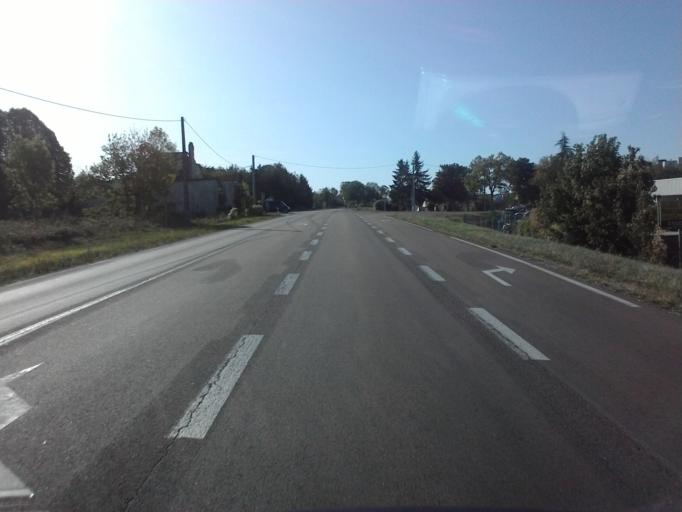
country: FR
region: Champagne-Ardenne
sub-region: Departement de l'Aube
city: Bar-sur-Seine
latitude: 48.0780
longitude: 4.3865
